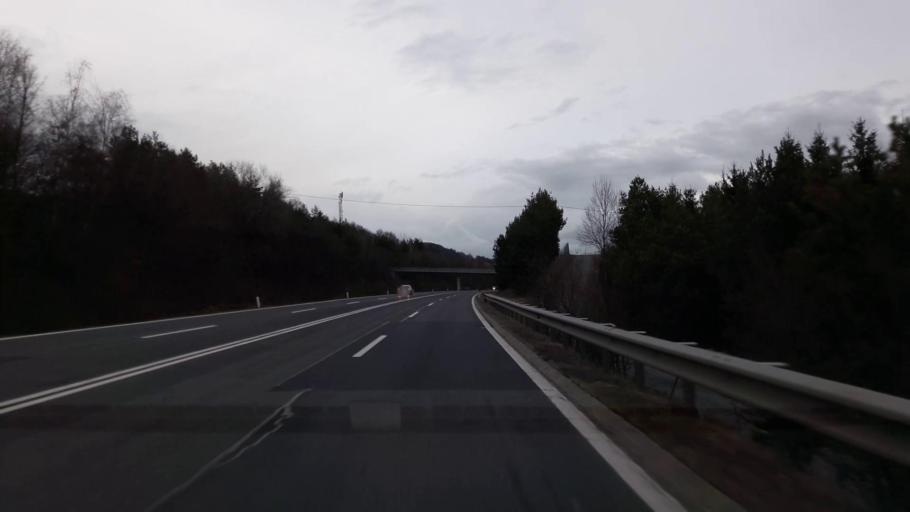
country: AT
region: Burgenland
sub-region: Politischer Bezirk Mattersburg
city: Sieggraben
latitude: 47.6447
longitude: 16.3740
